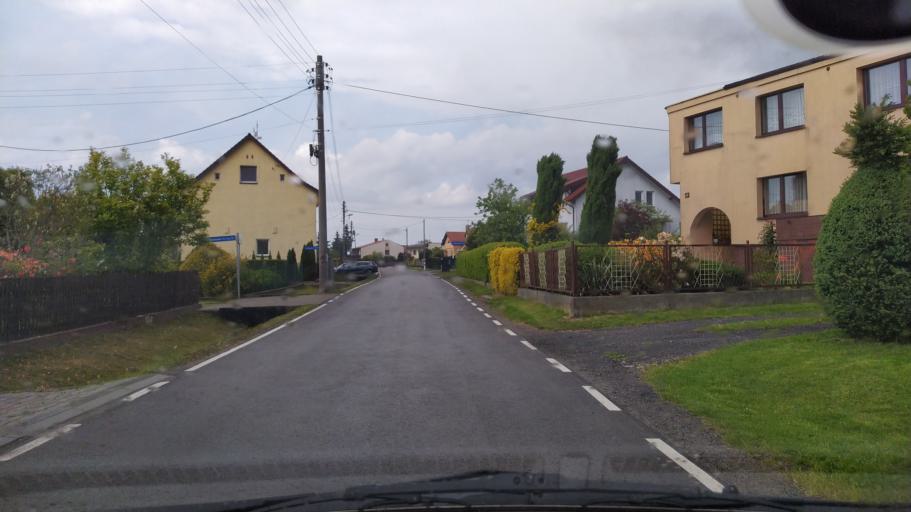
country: PL
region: Silesian Voivodeship
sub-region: Powiat gliwicki
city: Zernica
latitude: 50.2285
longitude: 18.6165
